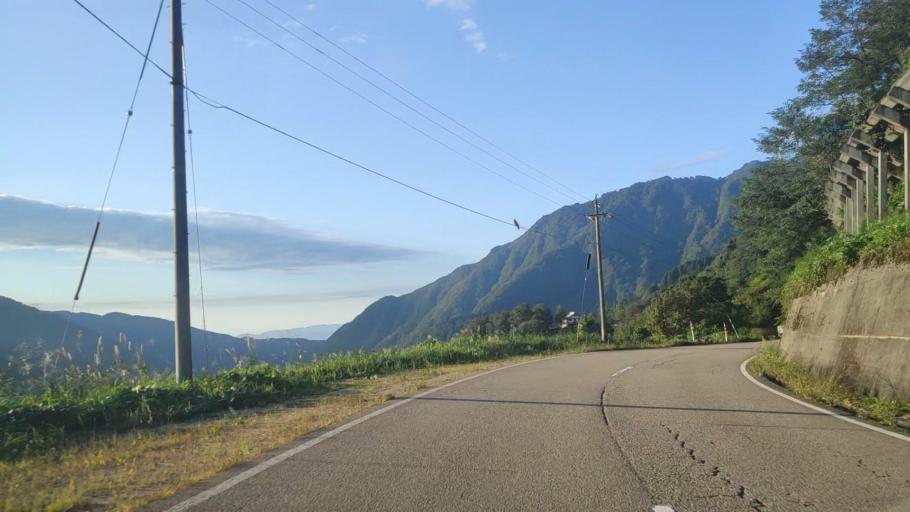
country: JP
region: Toyama
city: Yatsuomachi-higashikumisaka
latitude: 36.5202
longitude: 137.0281
